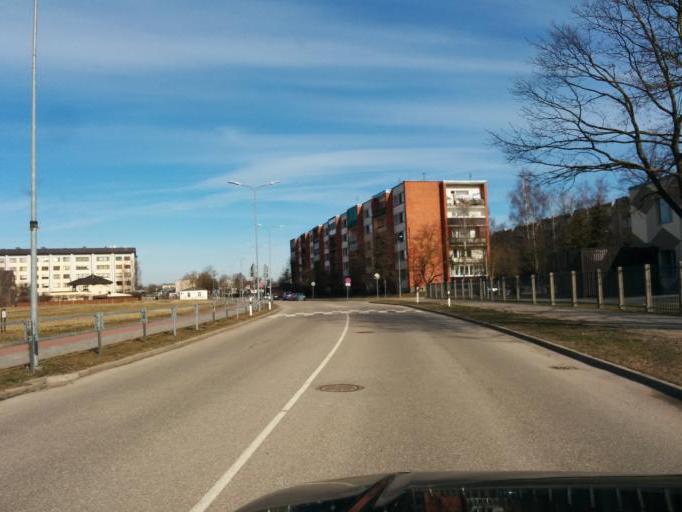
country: LV
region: Jelgava
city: Jelgava
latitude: 56.6404
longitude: 23.7200
